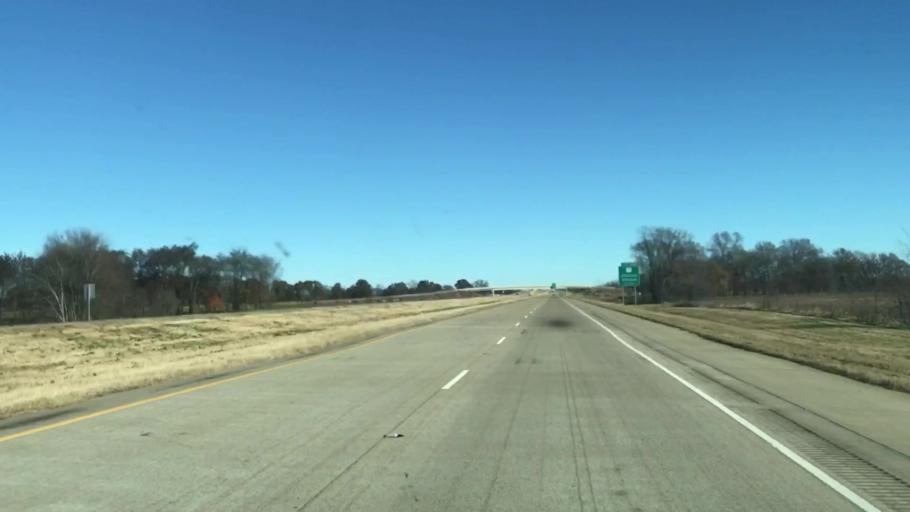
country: US
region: Louisiana
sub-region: Caddo Parish
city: Vivian
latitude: 32.8390
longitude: -93.8707
